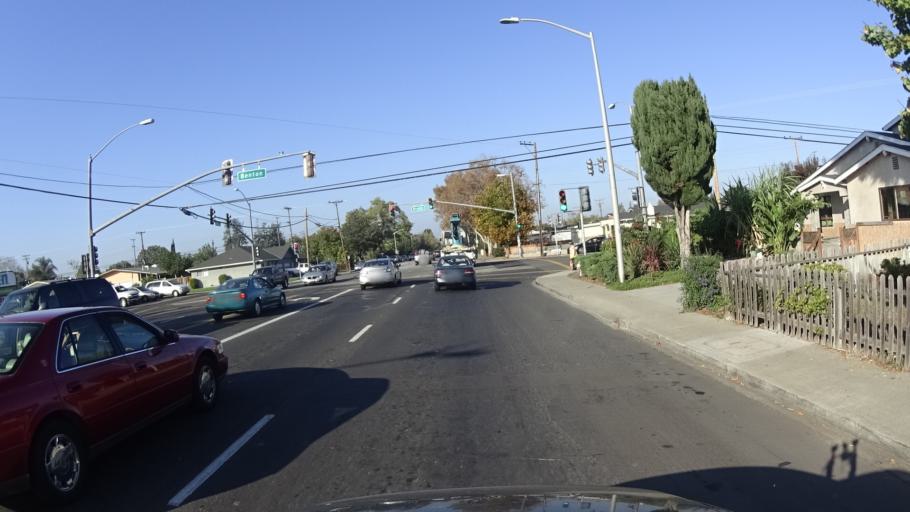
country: US
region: California
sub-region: Santa Clara County
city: Santa Clara
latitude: 37.3462
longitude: -121.9776
